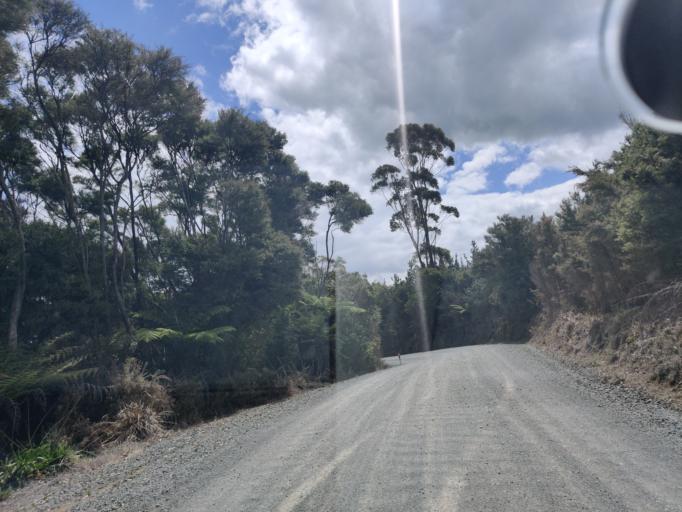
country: NZ
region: Northland
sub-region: Far North District
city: Paihia
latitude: -35.2598
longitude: 174.0534
